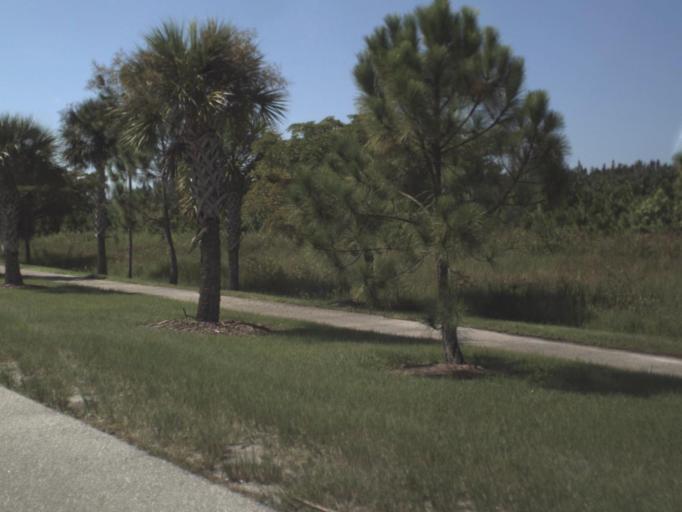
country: US
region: Florida
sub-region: Lee County
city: Pine Island Center
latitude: 26.6368
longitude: -82.0402
